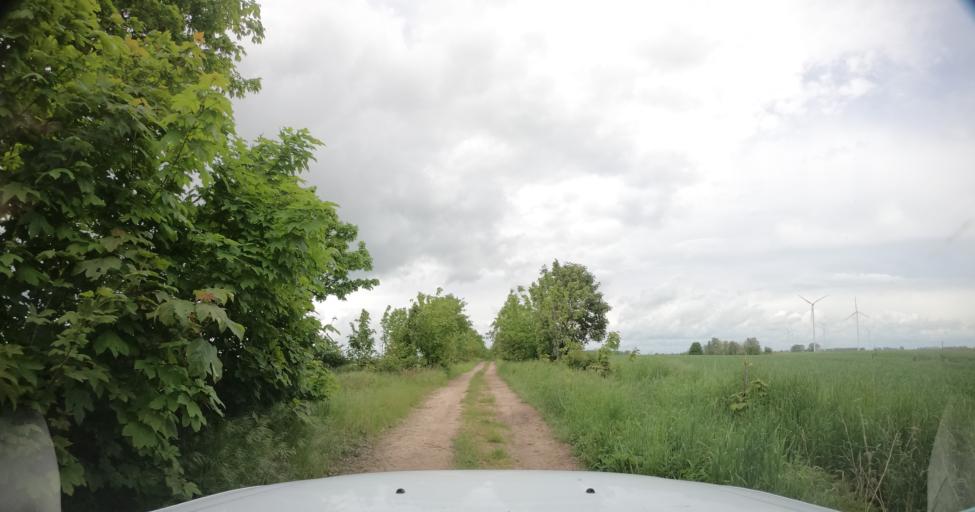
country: PL
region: West Pomeranian Voivodeship
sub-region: Powiat pyrzycki
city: Kozielice
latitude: 53.0853
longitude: 14.8250
